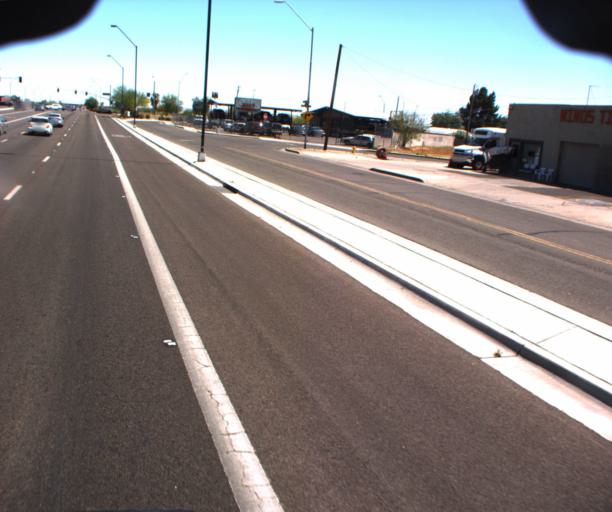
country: US
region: Arizona
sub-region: Maricopa County
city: Peoria
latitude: 33.5789
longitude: -112.2349
